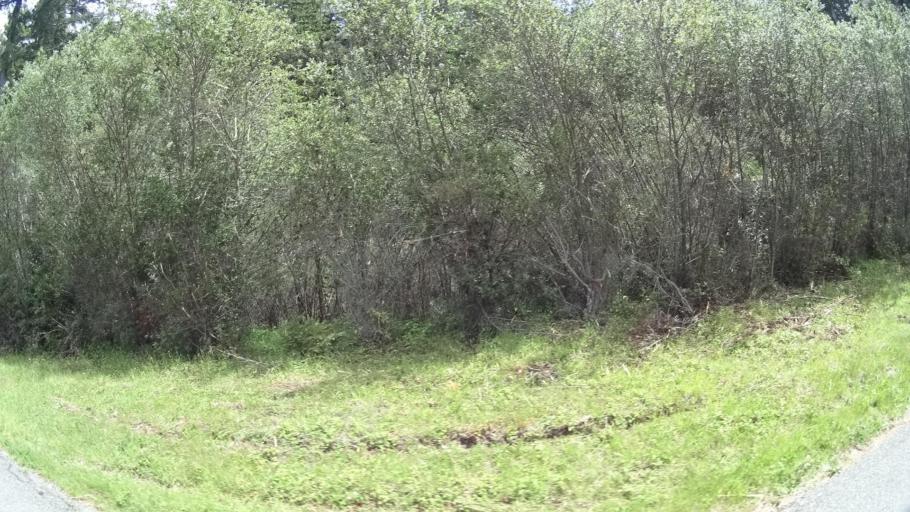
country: US
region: California
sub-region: Humboldt County
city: Blue Lake
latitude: 40.7808
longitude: -123.9628
